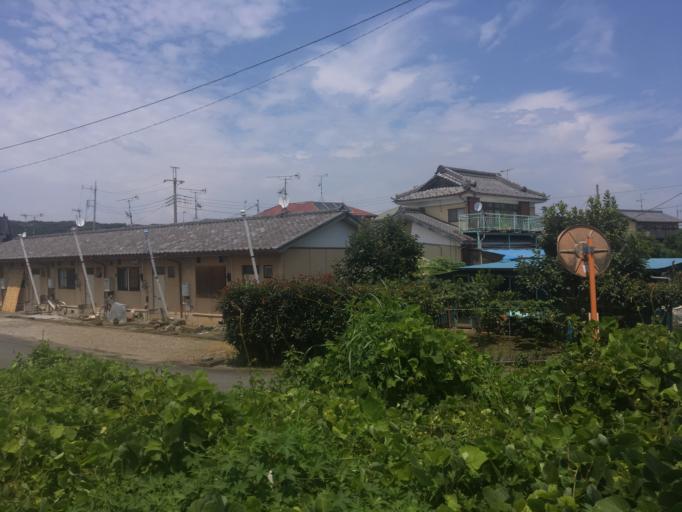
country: JP
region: Saitama
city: Kodamacho-kodamaminami
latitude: 36.1862
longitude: 139.1478
